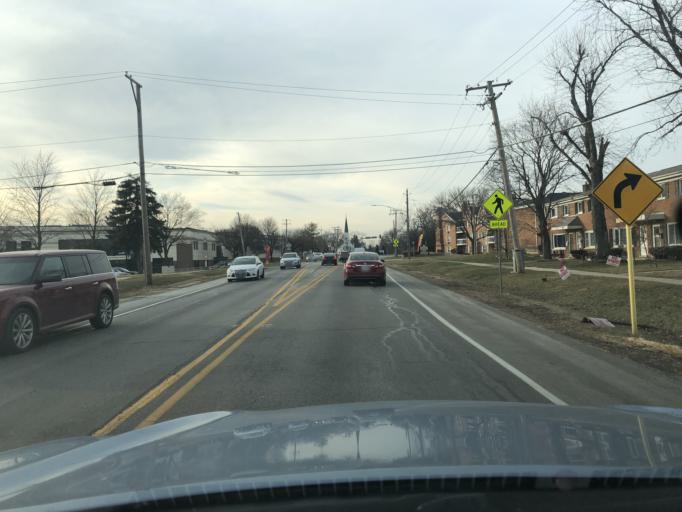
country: US
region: Illinois
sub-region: DuPage County
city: Itasca
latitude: 41.9682
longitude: -88.0083
